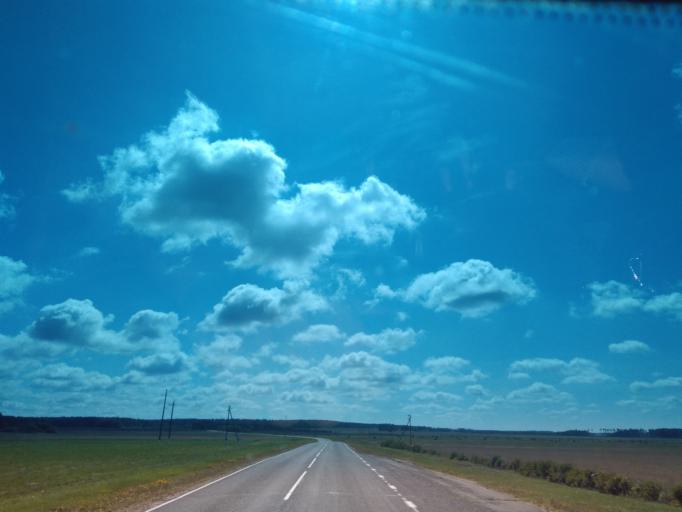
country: BY
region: Minsk
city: Uzda
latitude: 53.3991
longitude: 27.2290
